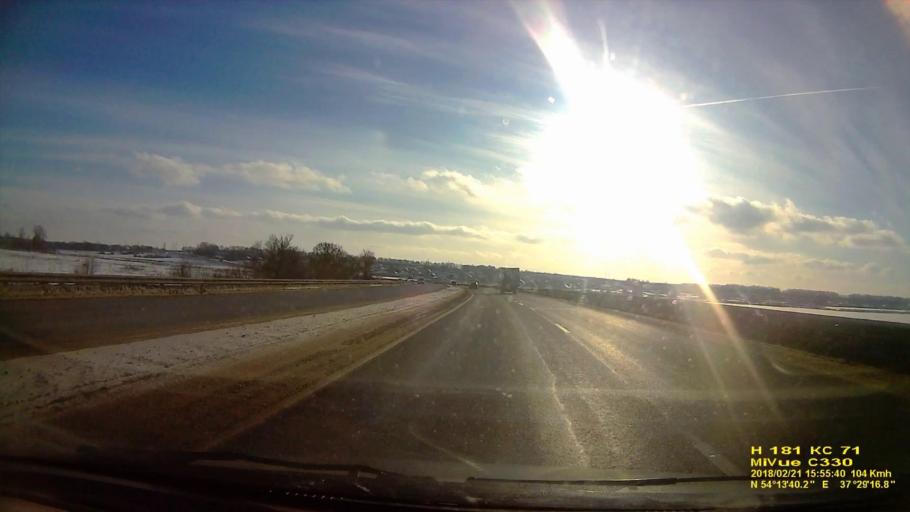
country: RU
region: Tula
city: Barsuki
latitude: 54.2277
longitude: 37.4878
